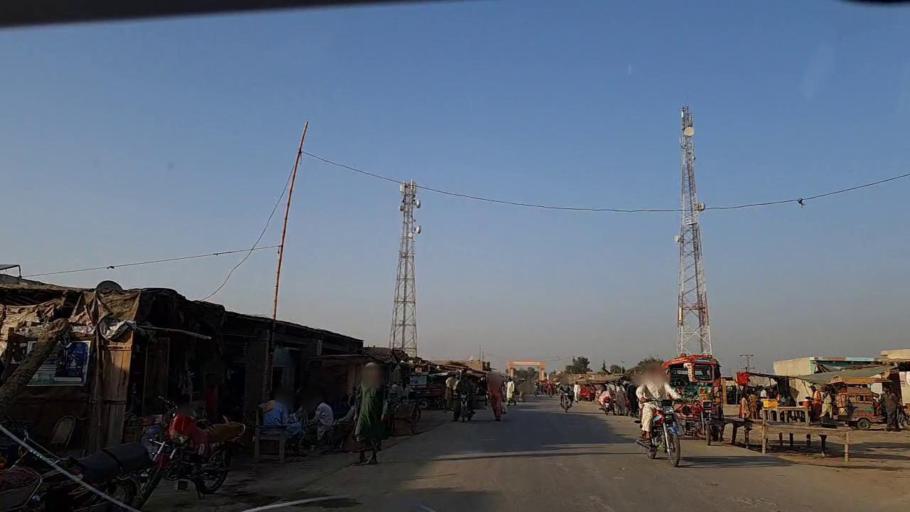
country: PK
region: Sindh
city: Rustam jo Goth
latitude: 28.0193
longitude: 68.8121
